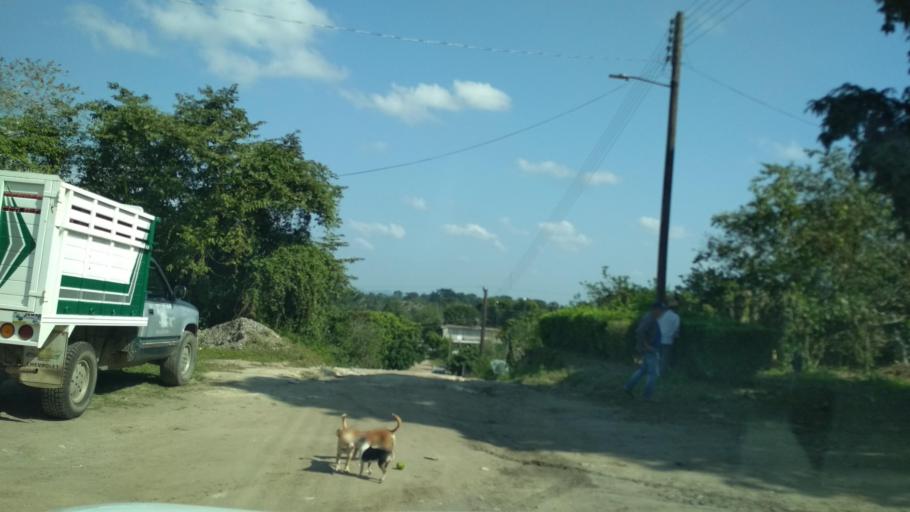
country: MX
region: Puebla
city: San Jose Acateno
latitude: 20.1892
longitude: -97.1574
